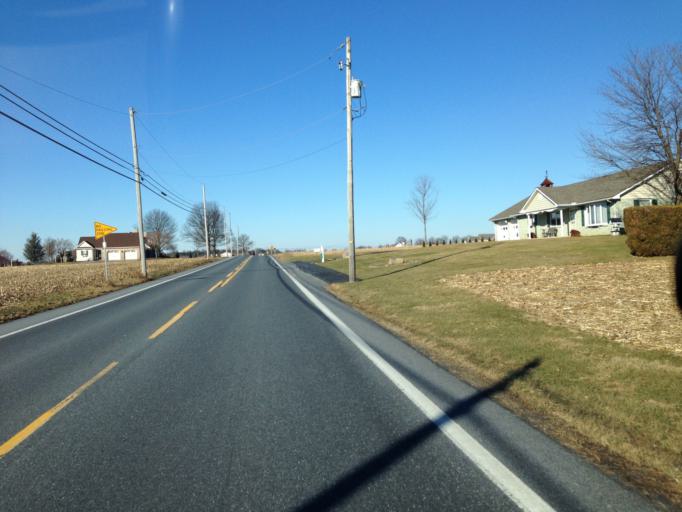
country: US
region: Pennsylvania
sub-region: Lancaster County
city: Lititz
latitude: 40.1722
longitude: -76.3330
